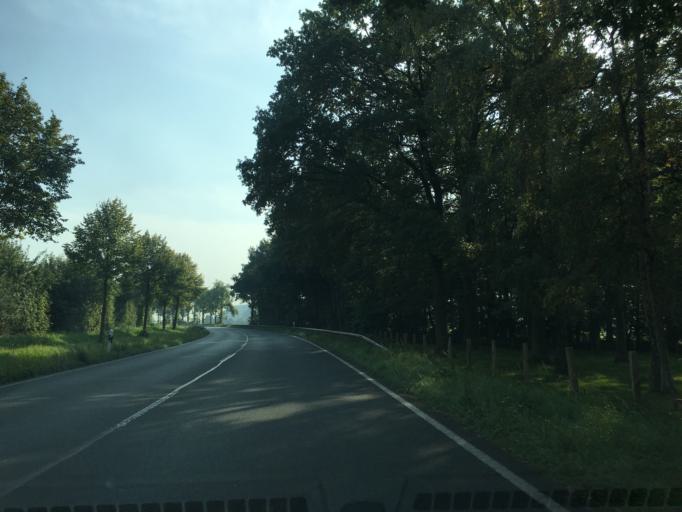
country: DE
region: North Rhine-Westphalia
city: Olfen
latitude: 51.7772
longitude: 7.3703
